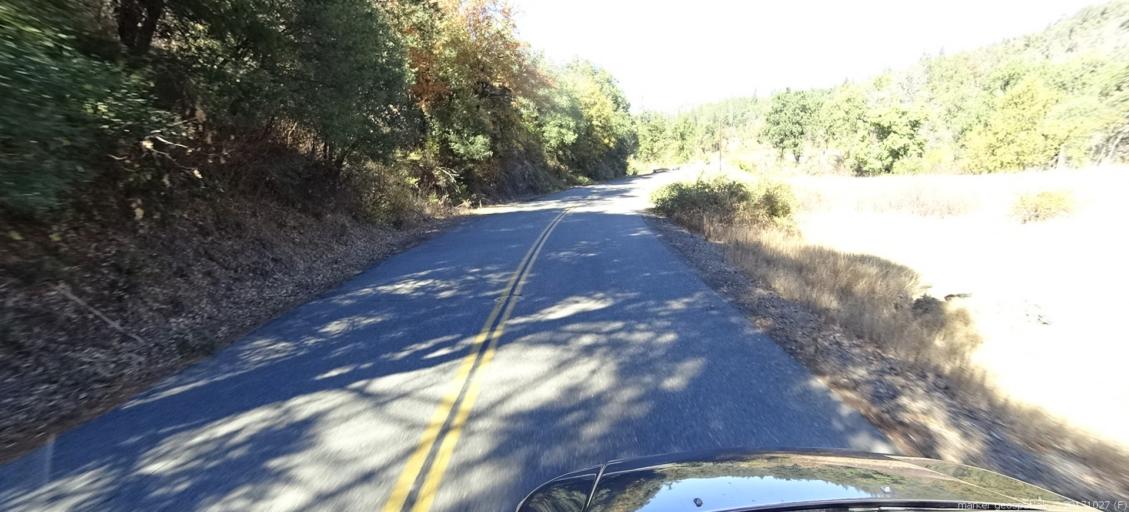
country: US
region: California
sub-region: Shasta County
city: Bella Vista
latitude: 40.7425
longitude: -122.0153
